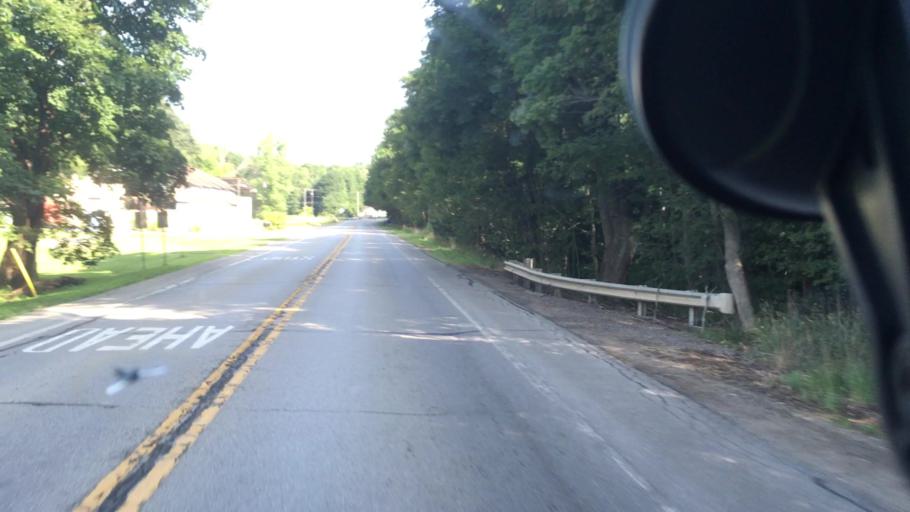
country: US
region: Pennsylvania
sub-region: Butler County
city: Slippery Rock
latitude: 41.0253
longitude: -80.1884
